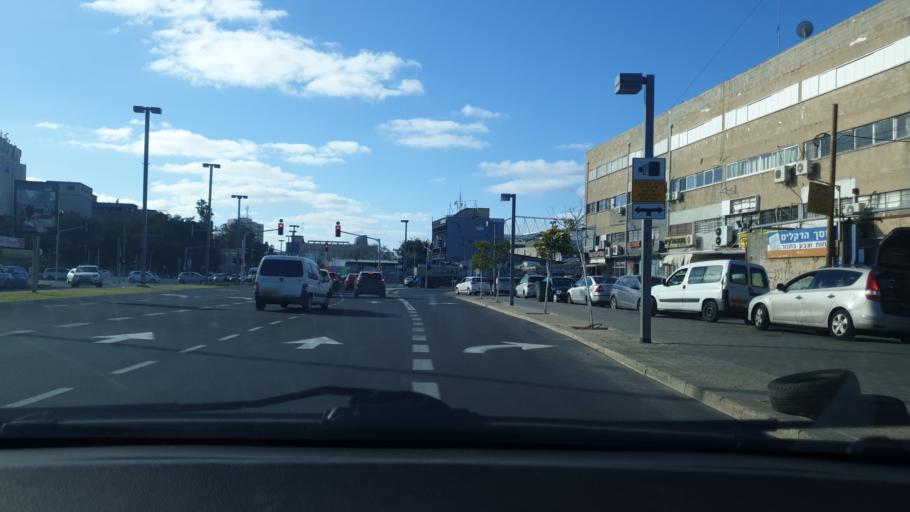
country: IL
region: Tel Aviv
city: Yafo
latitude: 32.0484
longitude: 34.7645
